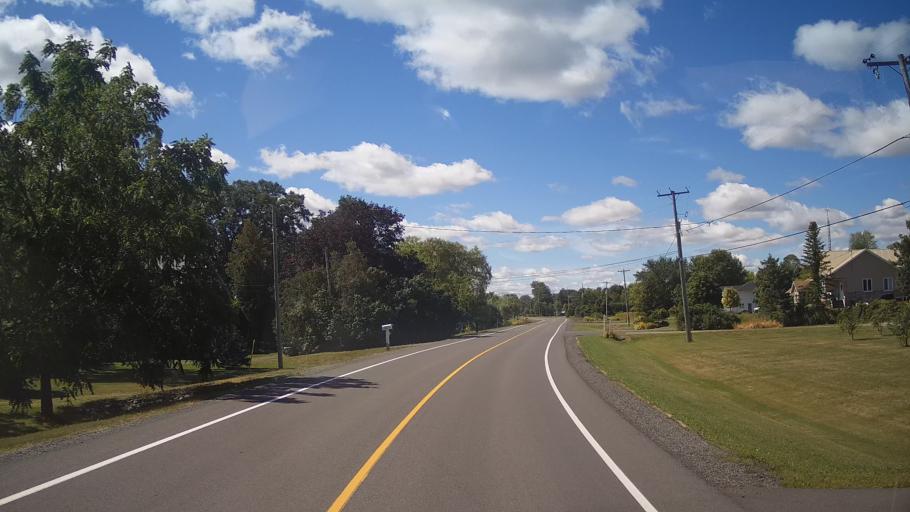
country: US
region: New York
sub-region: St. Lawrence County
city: Norfolk
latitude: 44.8677
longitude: -75.2490
